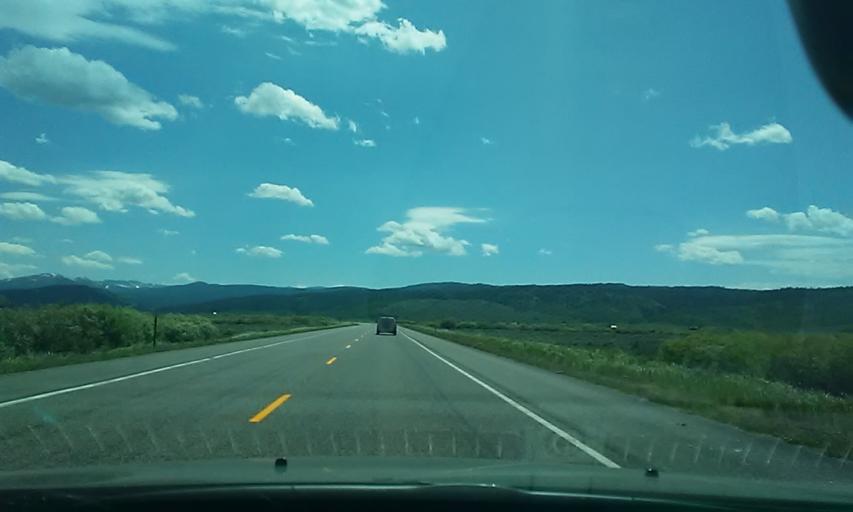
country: US
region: Wyoming
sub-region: Teton County
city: Jackson
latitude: 43.8343
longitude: -110.4282
